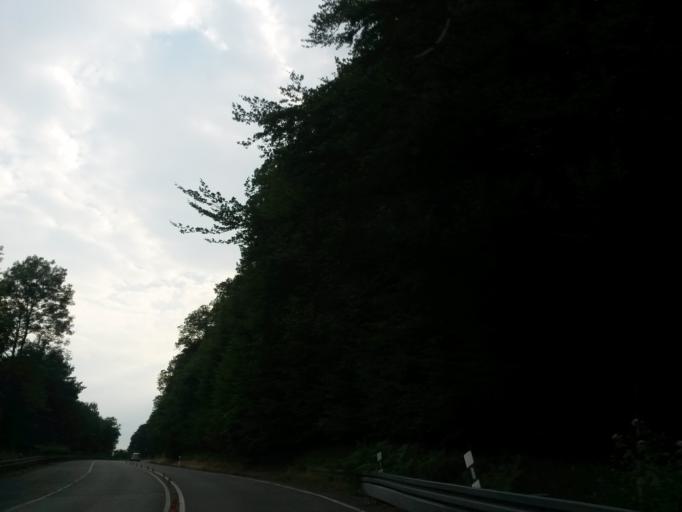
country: DE
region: North Rhine-Westphalia
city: Meinerzhagen
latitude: 51.0903
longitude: 7.6451
